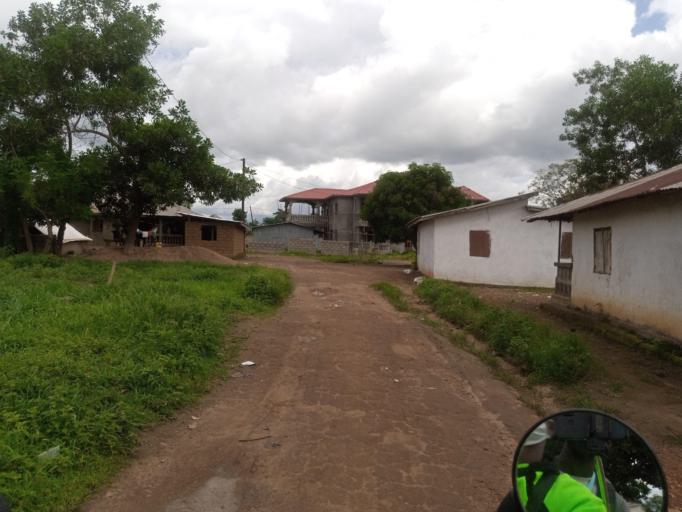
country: SL
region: Northern Province
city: Port Loko
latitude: 8.7754
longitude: -12.7730
